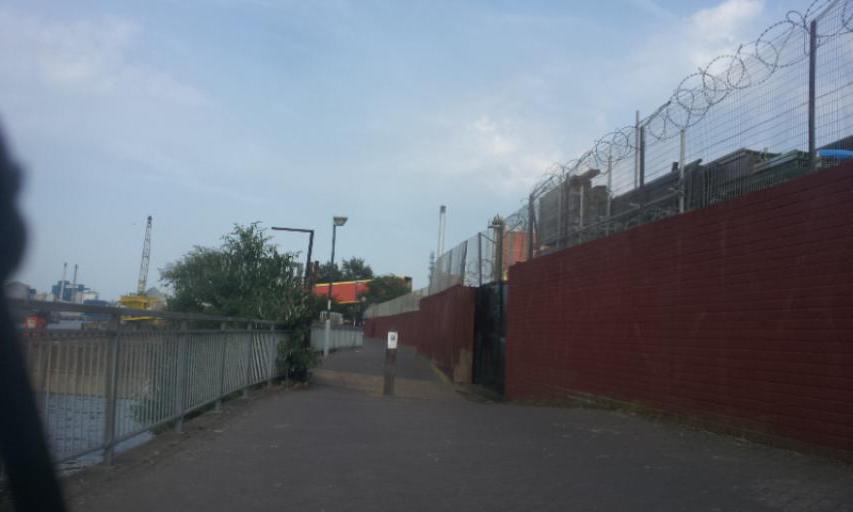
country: GB
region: England
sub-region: Greater London
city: Woolwich
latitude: 51.4941
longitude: 0.0315
